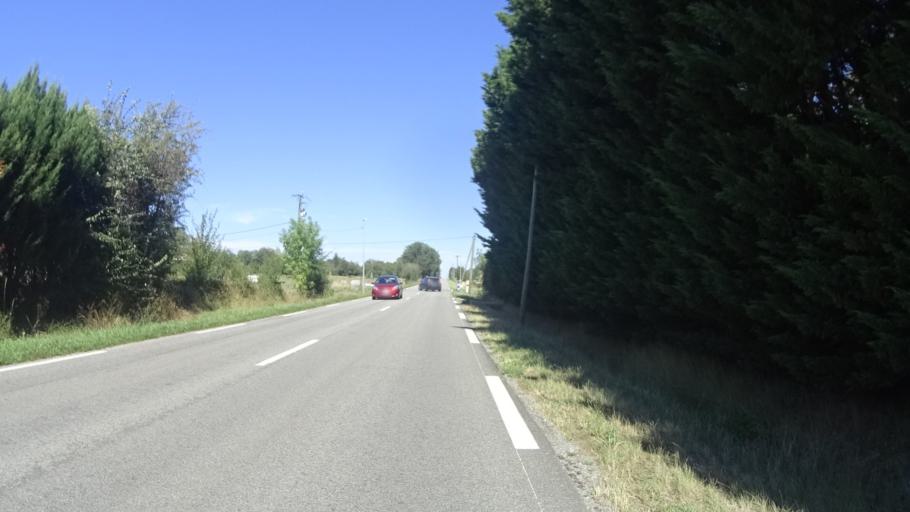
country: FR
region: Centre
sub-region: Departement du Cher
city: Belleville-sur-Loire
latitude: 47.5165
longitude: 2.8440
